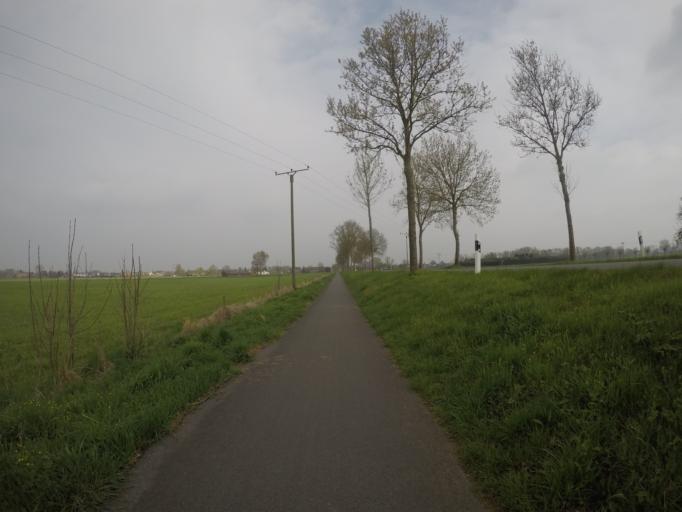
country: DE
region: North Rhine-Westphalia
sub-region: Regierungsbezirk Munster
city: Isselburg
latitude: 51.8534
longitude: 6.5037
